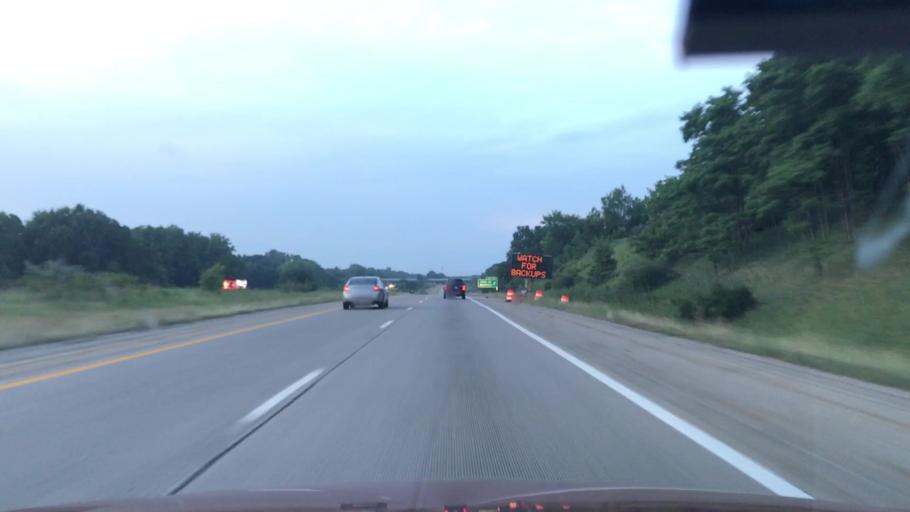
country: US
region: Michigan
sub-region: Kent County
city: Northview
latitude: 43.0801
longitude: -85.6372
